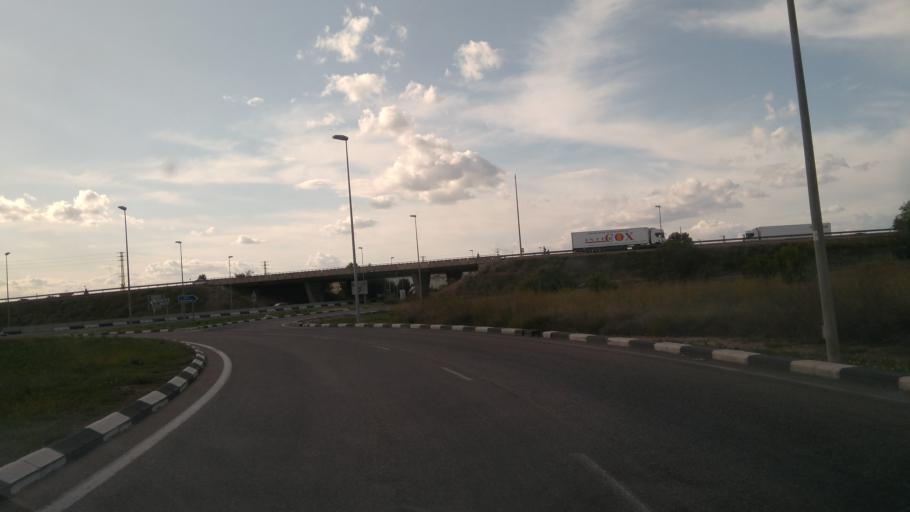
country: ES
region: Valencia
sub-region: Provincia de Valencia
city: L'Alcudia
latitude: 39.1935
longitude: -0.4936
